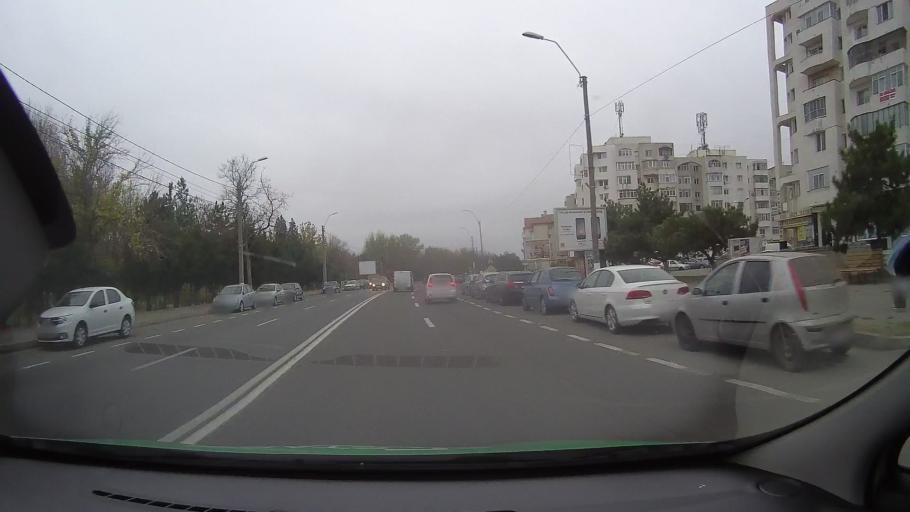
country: RO
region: Ialomita
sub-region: Comuna Slobozia
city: Slobozia
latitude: 44.5656
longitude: 27.3825
